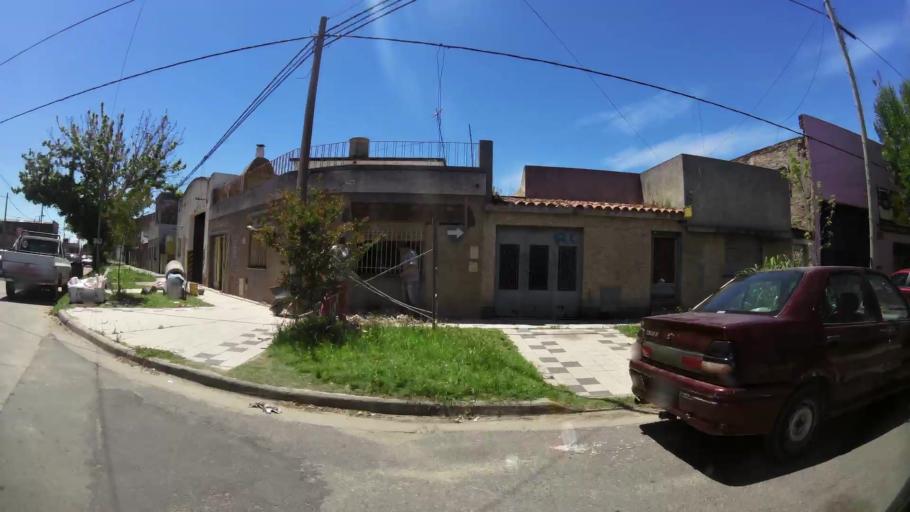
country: AR
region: Santa Fe
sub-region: Departamento de Rosario
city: Rosario
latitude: -32.9453
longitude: -60.7112
